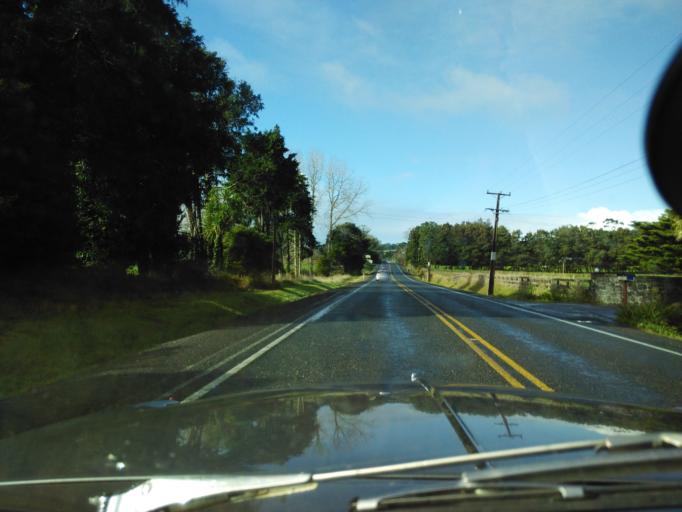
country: NZ
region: Auckland
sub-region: Auckland
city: Parakai
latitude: -36.6410
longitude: 174.5722
